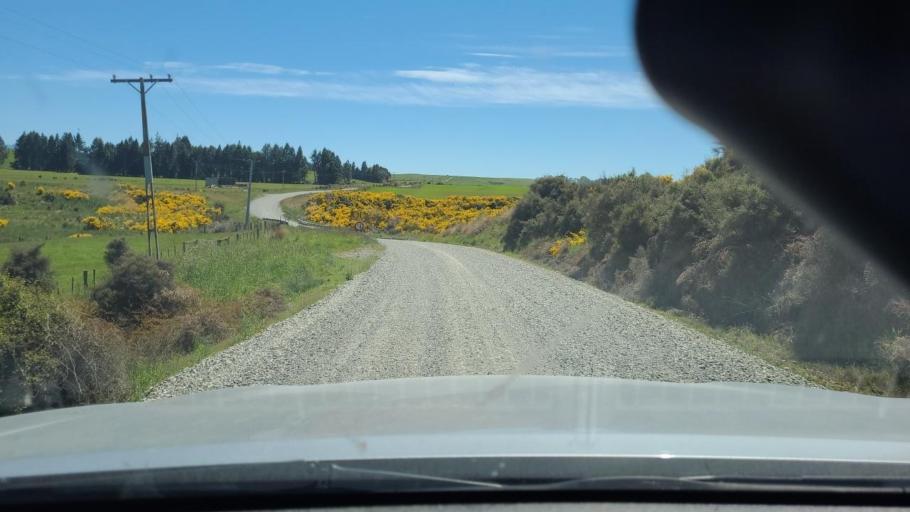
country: NZ
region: Southland
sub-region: Southland District
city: Te Anau
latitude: -45.4955
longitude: 167.8930
